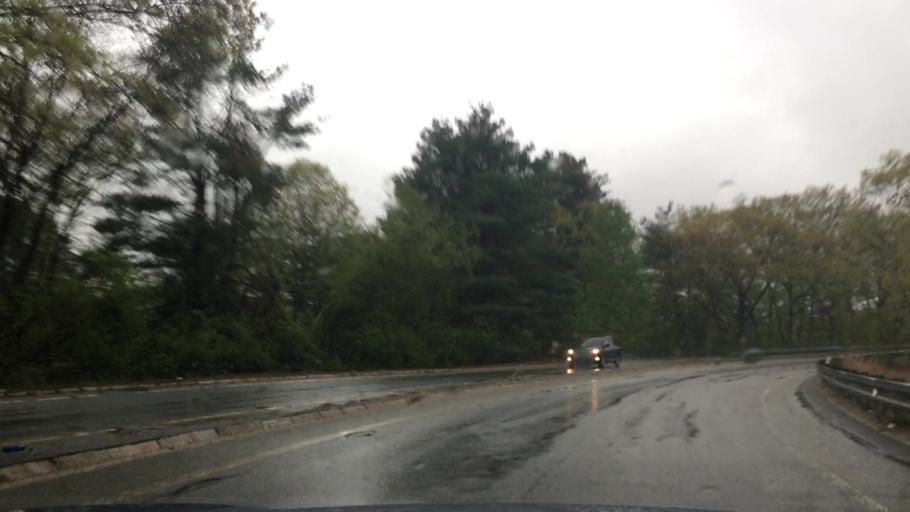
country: US
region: Massachusetts
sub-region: Middlesex County
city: Lowell
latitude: 42.5875
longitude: -71.3142
